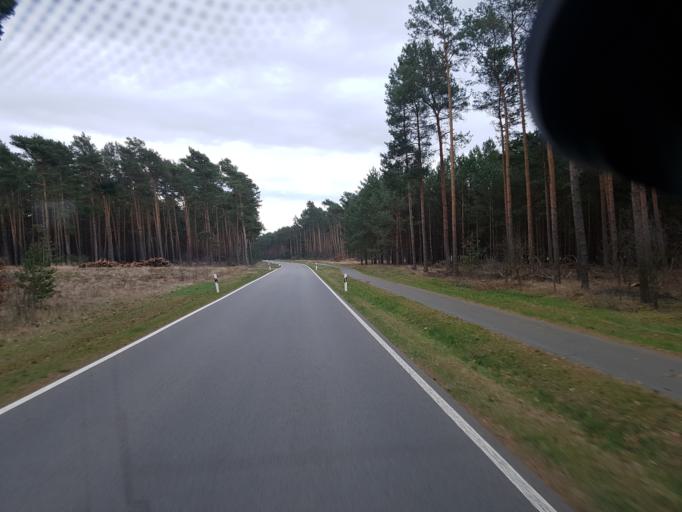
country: DE
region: Brandenburg
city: Mixdorf
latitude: 52.2008
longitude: 14.3756
